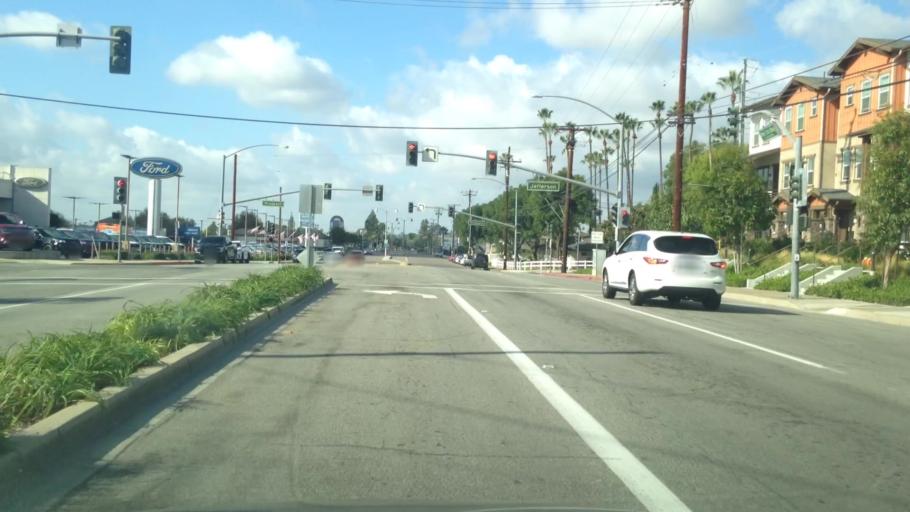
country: US
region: California
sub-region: Orange County
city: Yorba Linda
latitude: 33.8884
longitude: -117.8369
